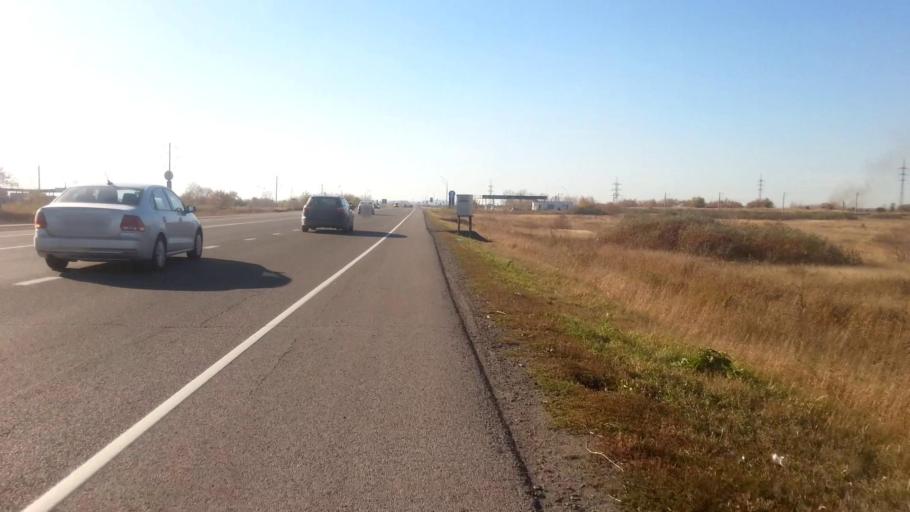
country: RU
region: Altai Krai
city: Novoaltaysk
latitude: 53.3731
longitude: 83.9508
